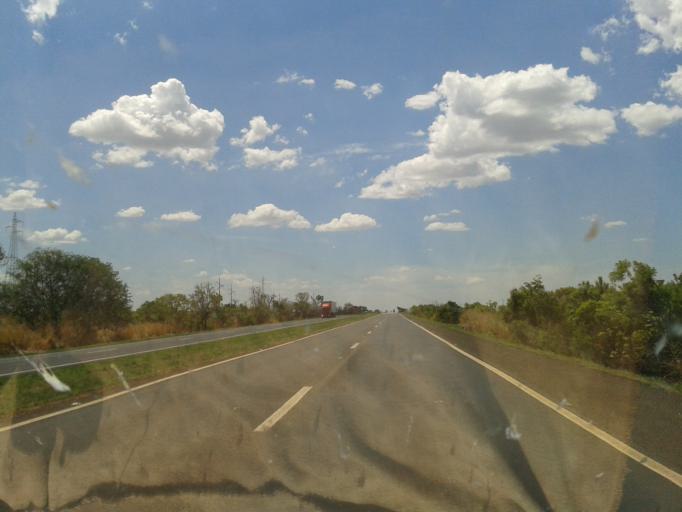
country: BR
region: Minas Gerais
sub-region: Uberlandia
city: Uberlandia
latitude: -19.0581
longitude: -48.1940
